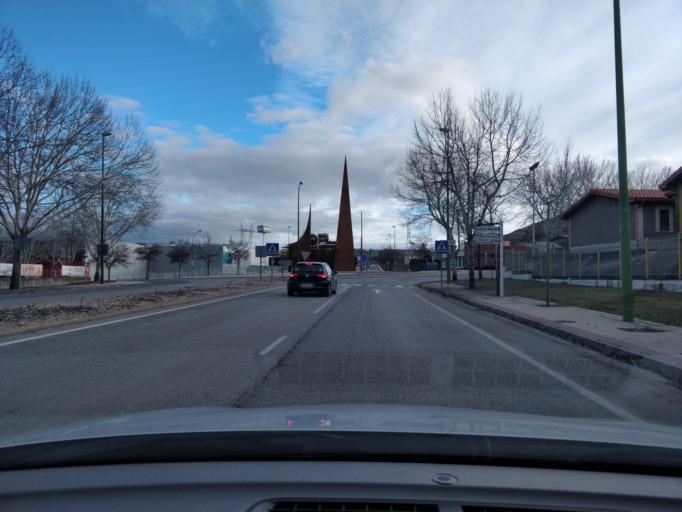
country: ES
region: Castille and Leon
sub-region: Provincia de Burgos
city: Sotragero
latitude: 42.3669
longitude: -3.7150
